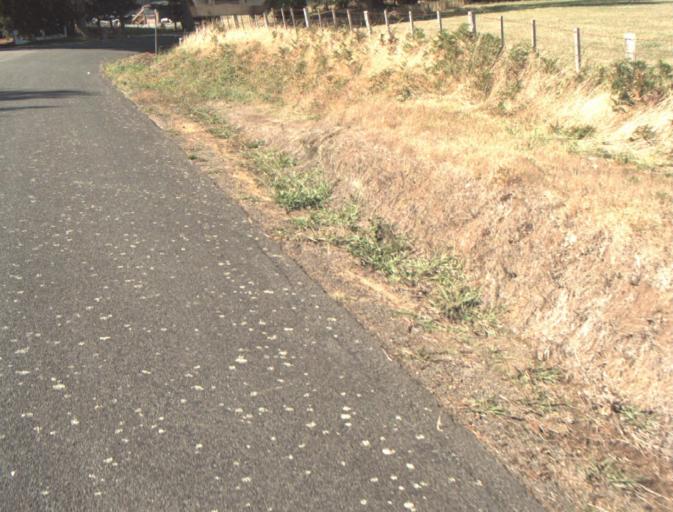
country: AU
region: Tasmania
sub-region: Launceston
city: Mayfield
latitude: -41.2863
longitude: 147.2140
